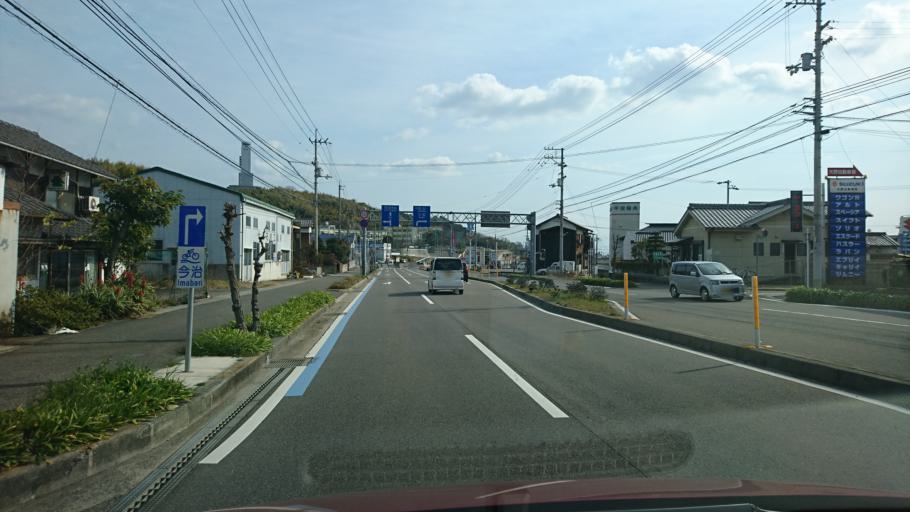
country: JP
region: Ehime
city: Hojo
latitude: 34.0907
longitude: 132.9818
